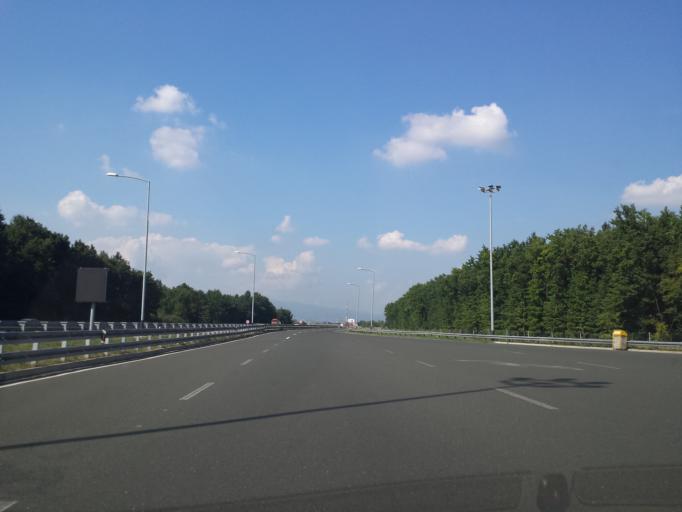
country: HR
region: Grad Zagreb
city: Brezovica
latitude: 45.7246
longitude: 15.8707
